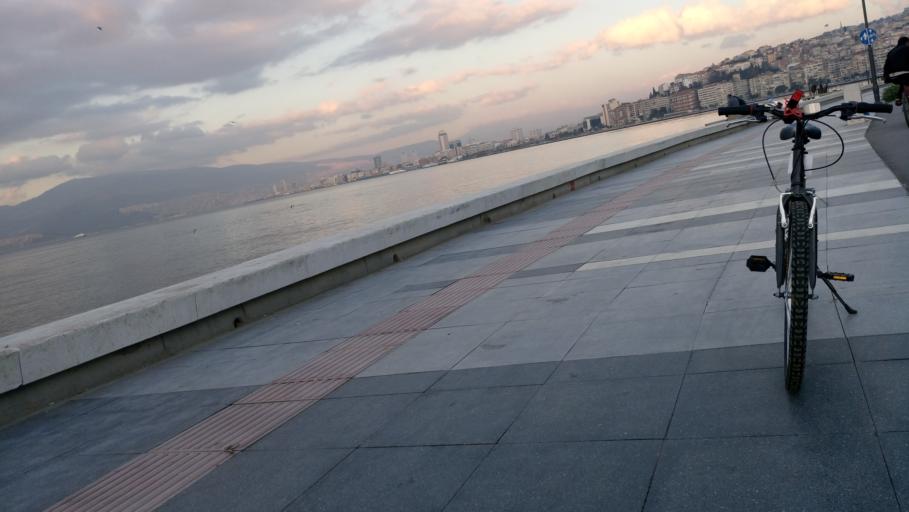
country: TR
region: Izmir
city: Izmir
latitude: 38.4101
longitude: 27.1110
